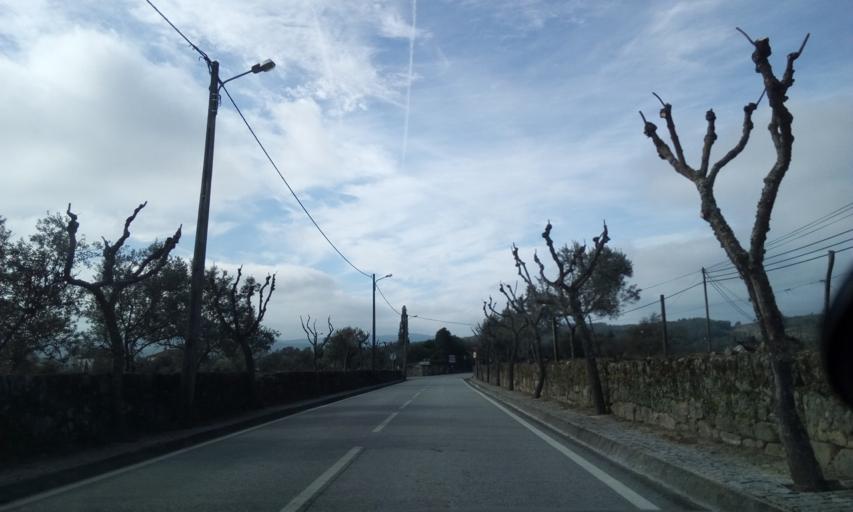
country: PT
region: Guarda
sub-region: Aguiar da Beira
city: Aguiar da Beira
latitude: 40.7357
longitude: -7.5562
